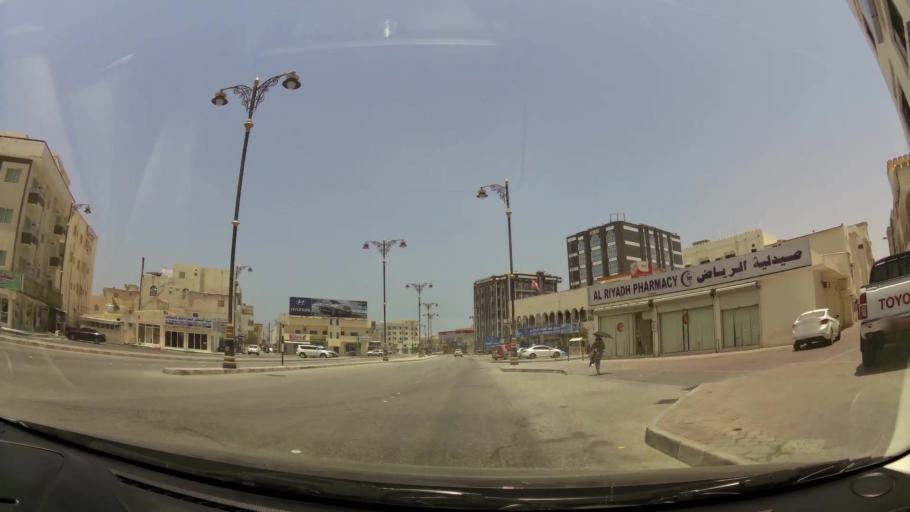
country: OM
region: Zufar
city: Salalah
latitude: 17.0172
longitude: 54.1102
